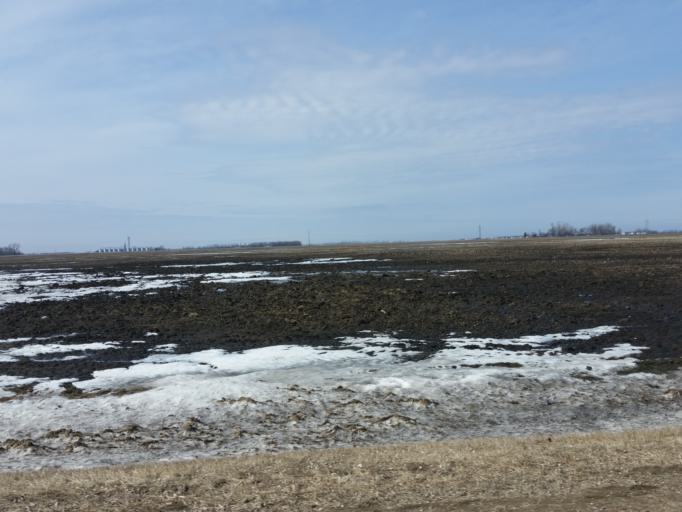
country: US
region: North Dakota
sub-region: Walsh County
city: Grafton
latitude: 48.2983
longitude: -97.2548
